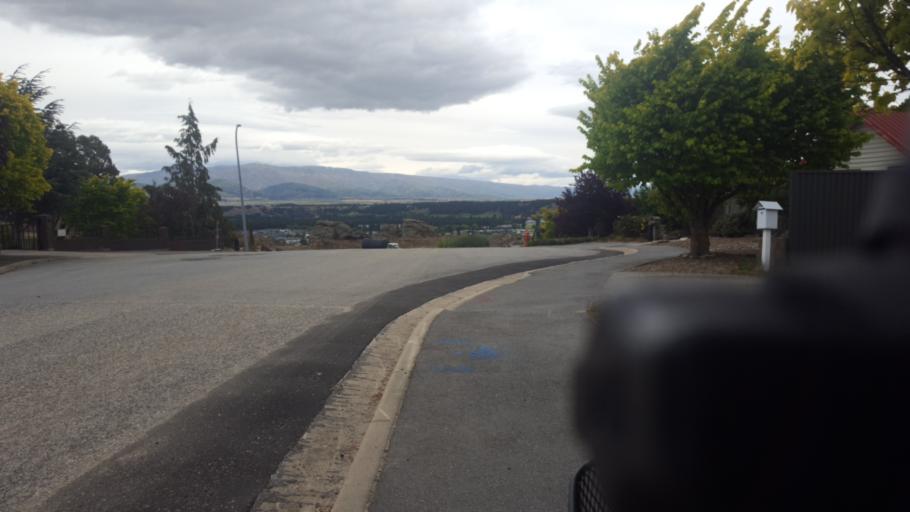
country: NZ
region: Otago
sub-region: Queenstown-Lakes District
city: Wanaka
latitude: -45.2611
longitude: 169.3776
